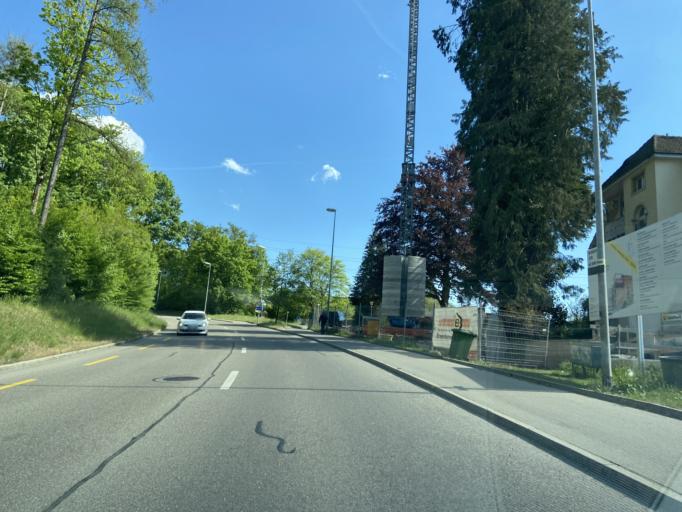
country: CH
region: Zurich
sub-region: Bezirk Buelach
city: Rorbas
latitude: 47.5238
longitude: 8.5811
